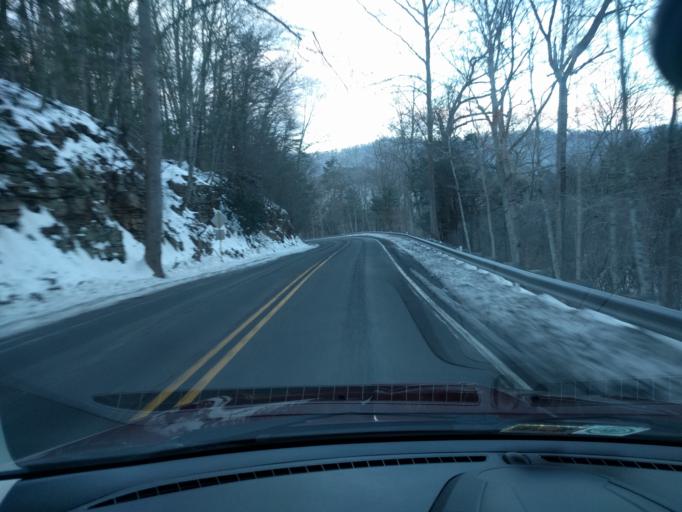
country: US
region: Virginia
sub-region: Bath County
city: Warm Springs
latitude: 38.0711
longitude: -79.8334
